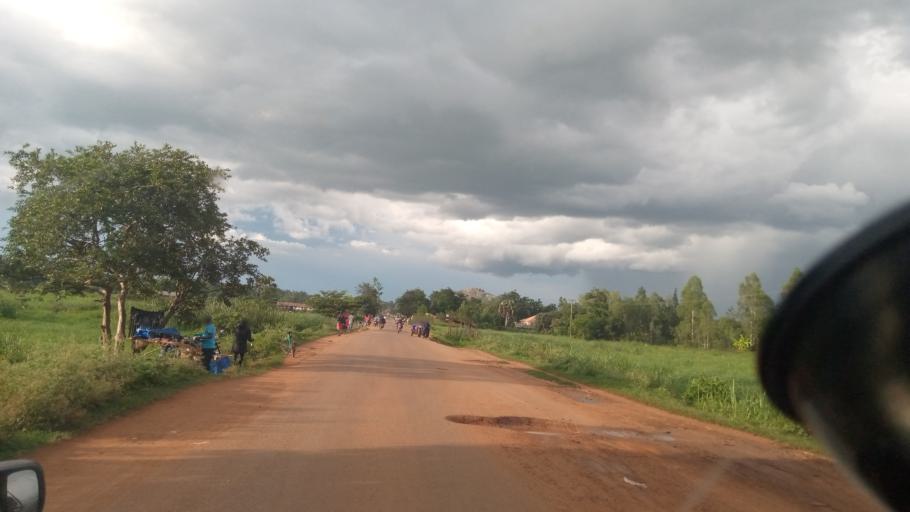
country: UG
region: Northern Region
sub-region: Lira District
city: Lira
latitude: 2.2659
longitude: 32.9119
